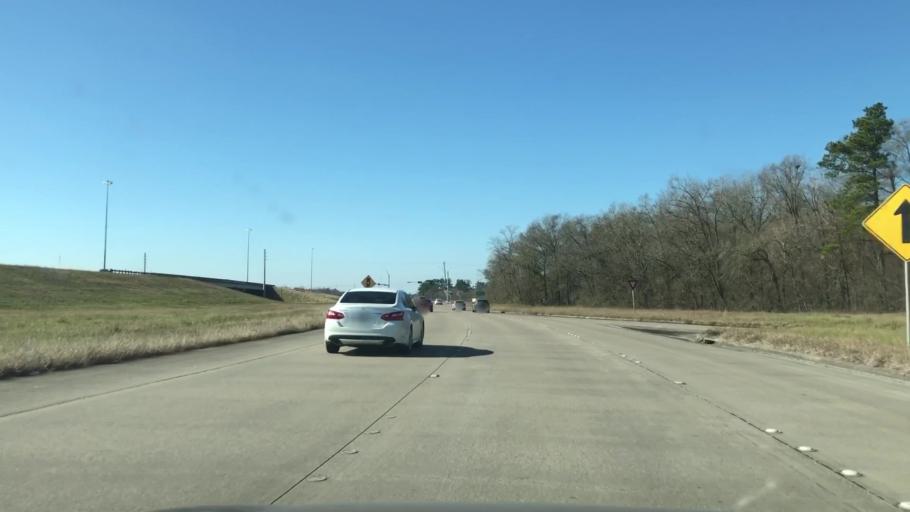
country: US
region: Texas
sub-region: Harris County
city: Cloverleaf
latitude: 29.8316
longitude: -95.1801
